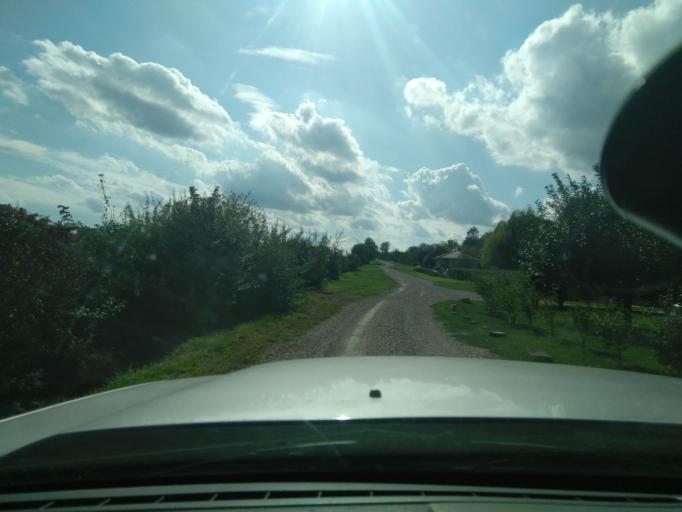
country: HU
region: Fejer
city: Bicske
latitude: 47.4837
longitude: 18.6528
